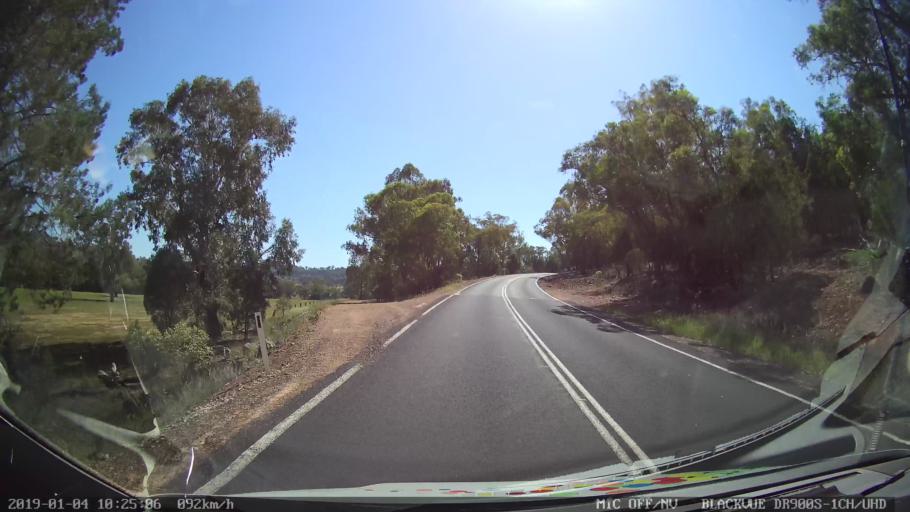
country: AU
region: New South Wales
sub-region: Cabonne
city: Canowindra
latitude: -33.3683
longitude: 148.5654
